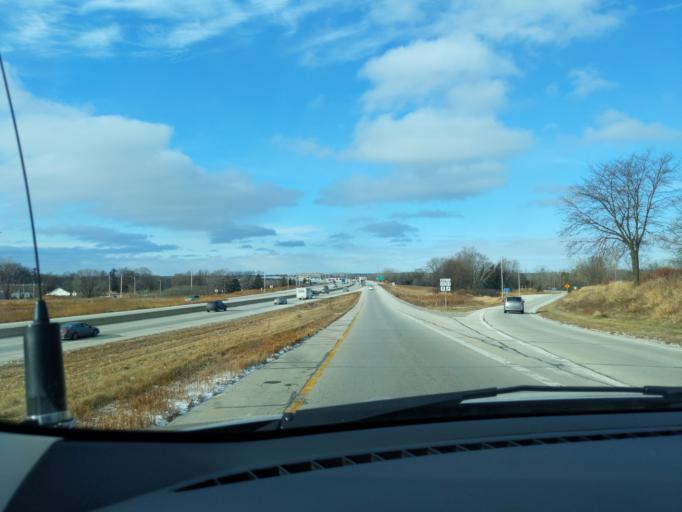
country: US
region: Wisconsin
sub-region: Brown County
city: Allouez
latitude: 44.4720
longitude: -88.0326
